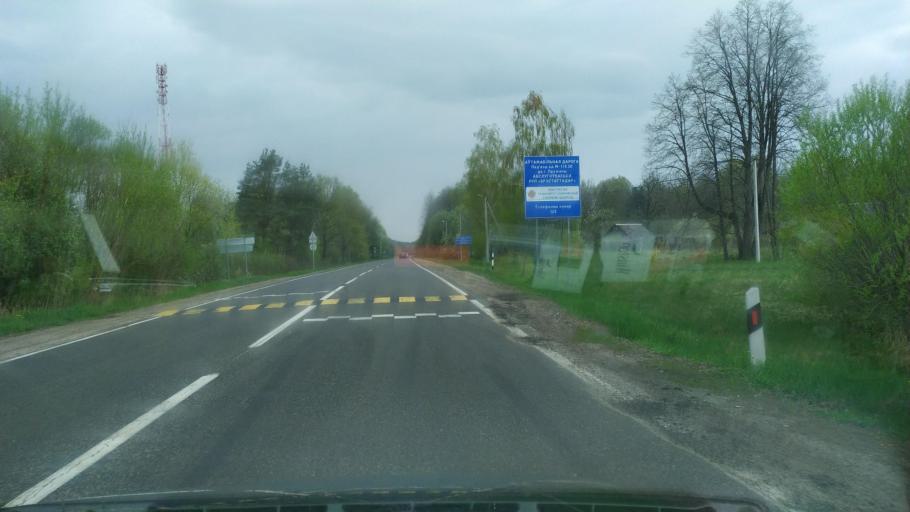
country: BY
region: Brest
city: Horad Kobryn
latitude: 52.3300
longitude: 24.5775
